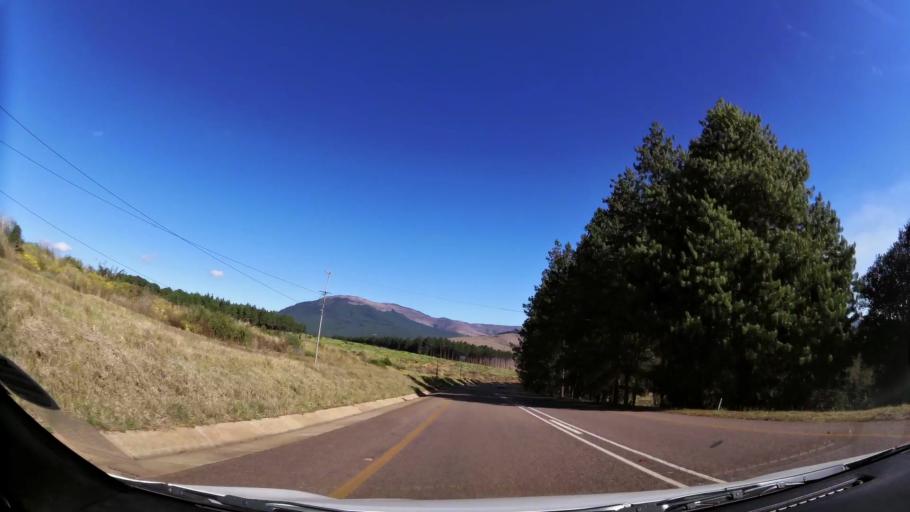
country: ZA
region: Limpopo
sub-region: Capricorn District Municipality
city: Mankoeng
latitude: -23.9323
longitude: 29.9561
